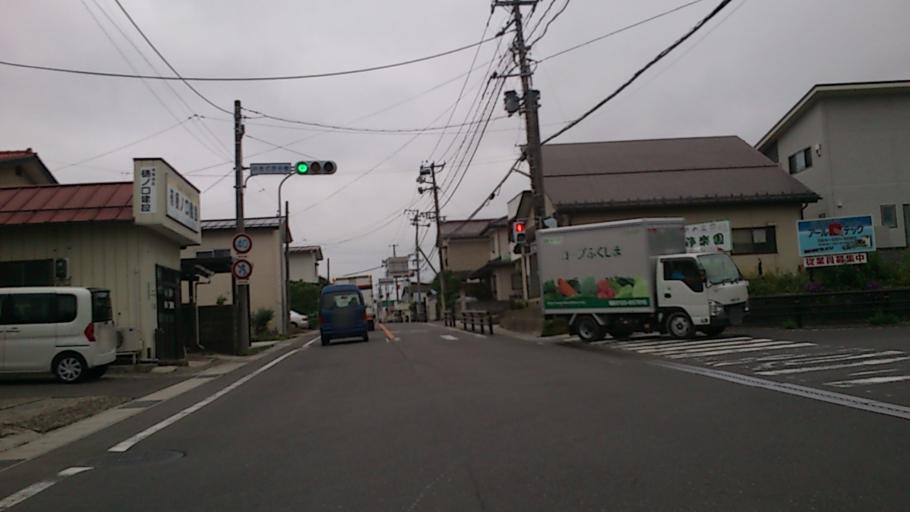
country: JP
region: Fukushima
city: Fukushima-shi
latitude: 37.8190
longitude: 140.4467
